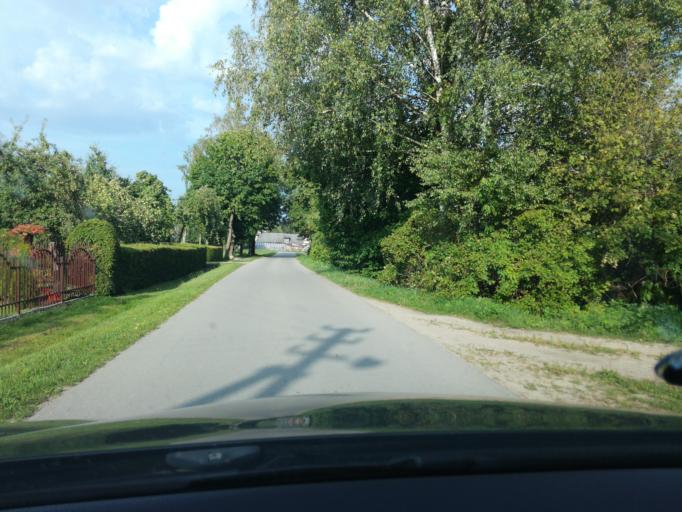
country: LT
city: Simnas
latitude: 54.3844
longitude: 23.6848
